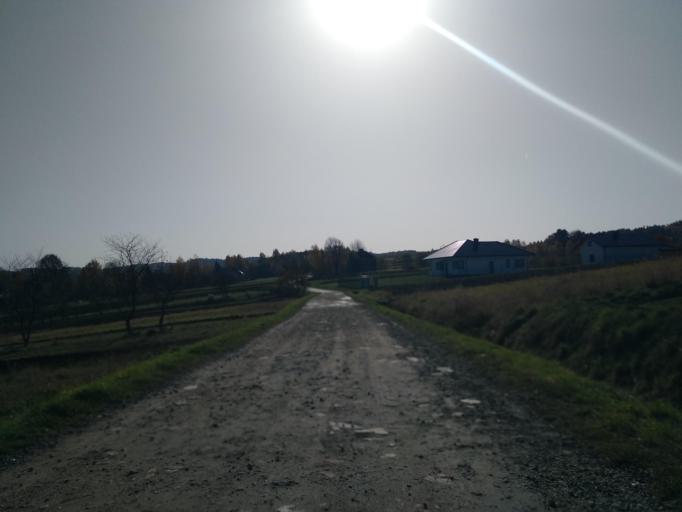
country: PL
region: Subcarpathian Voivodeship
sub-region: Powiat rzeszowski
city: Blazowa
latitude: 49.8665
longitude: 22.1227
